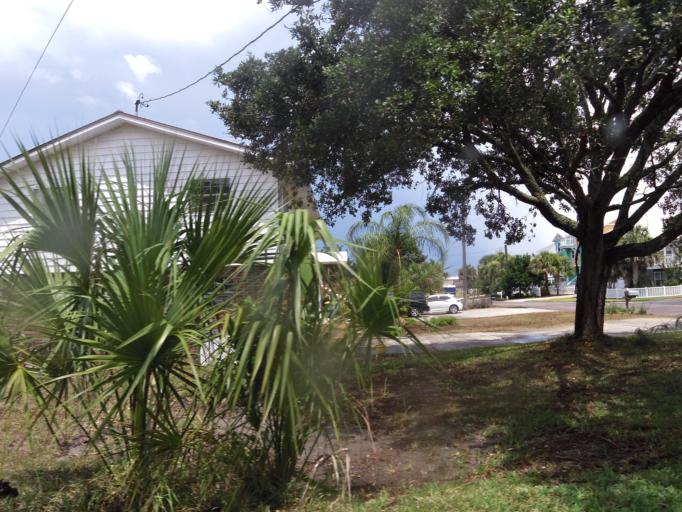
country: US
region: Florida
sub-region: Nassau County
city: Fernandina Beach
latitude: 30.6775
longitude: -81.4335
